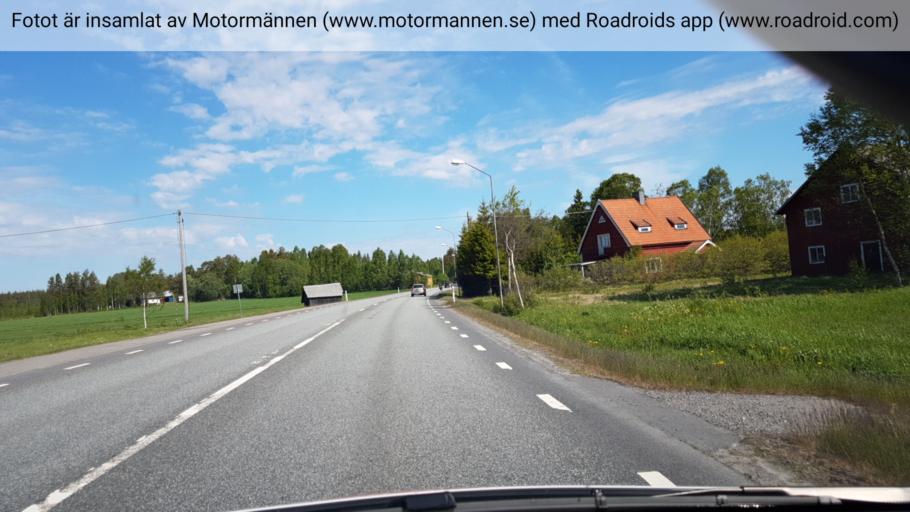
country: SE
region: Vaesterbotten
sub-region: Skelleftea Kommun
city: Burea
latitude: 64.5086
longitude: 21.2571
